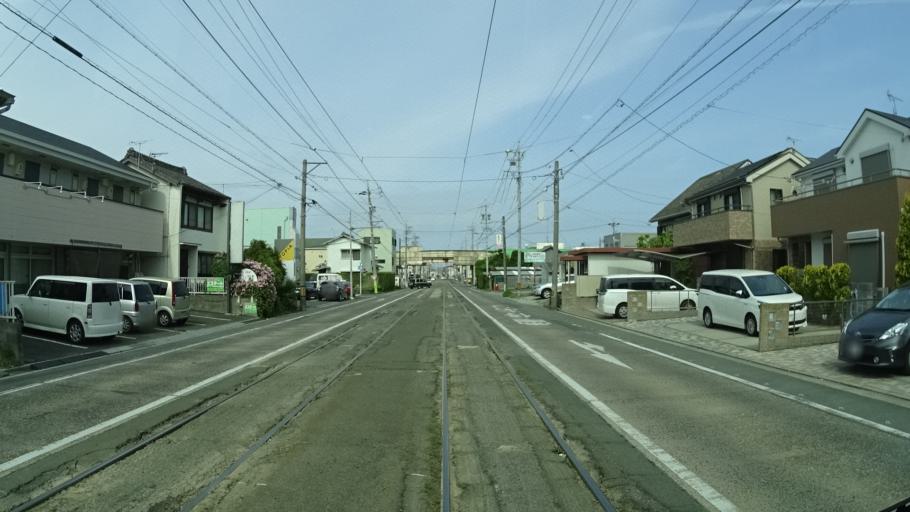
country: JP
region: Aichi
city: Toyohashi
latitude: 34.7654
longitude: 137.4122
